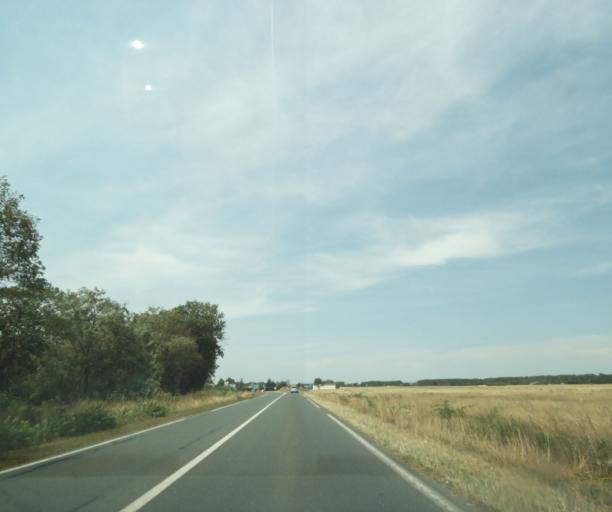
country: FR
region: Poitou-Charentes
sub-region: Departement de la Vienne
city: Cenon-sur-Vienne
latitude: 46.7756
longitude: 0.5495
